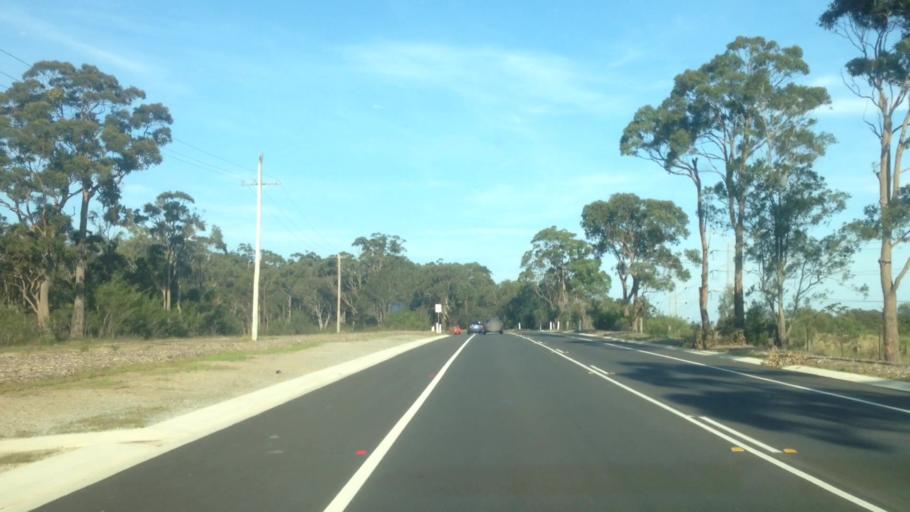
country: AU
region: New South Wales
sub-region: Wyong Shire
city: Kingfisher Shores
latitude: -33.1570
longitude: 151.4818
